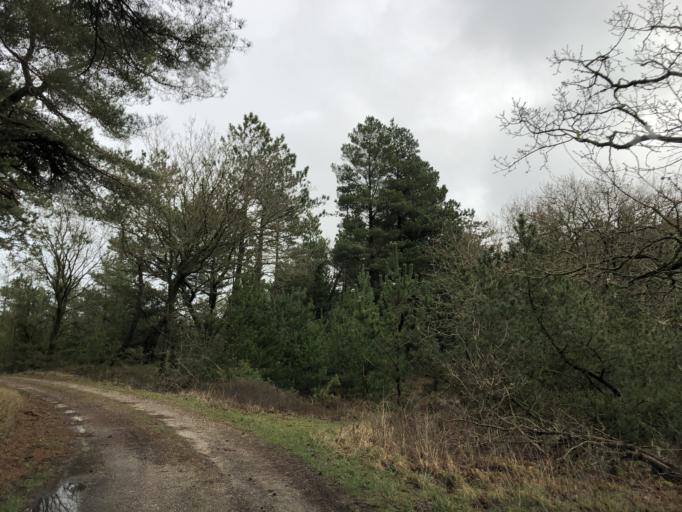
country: DK
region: Central Jutland
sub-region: Holstebro Kommune
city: Ulfborg
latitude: 56.2923
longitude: 8.1767
